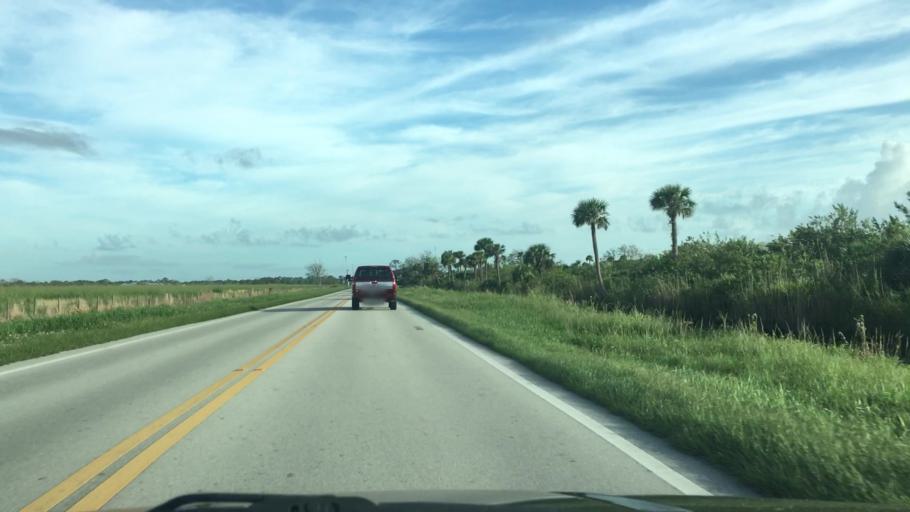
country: US
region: Florida
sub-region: Indian River County
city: Winter Beach
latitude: 27.7011
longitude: -80.4626
